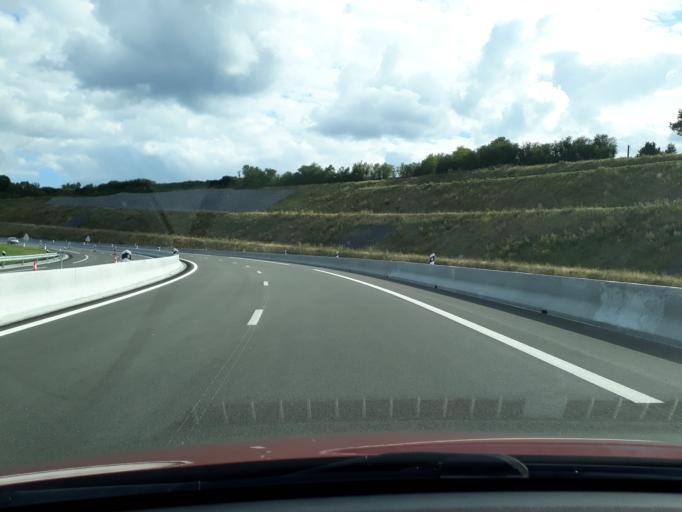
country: FR
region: Auvergne
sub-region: Departement de la Haute-Loire
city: Chadrac
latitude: 45.0491
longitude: 3.9026
